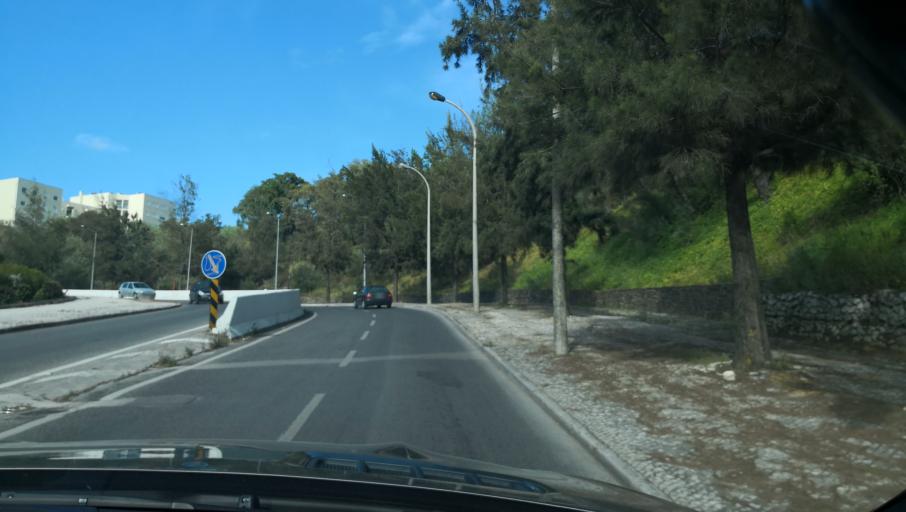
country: PT
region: Setubal
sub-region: Setubal
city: Setubal
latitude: 38.5201
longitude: -8.8757
